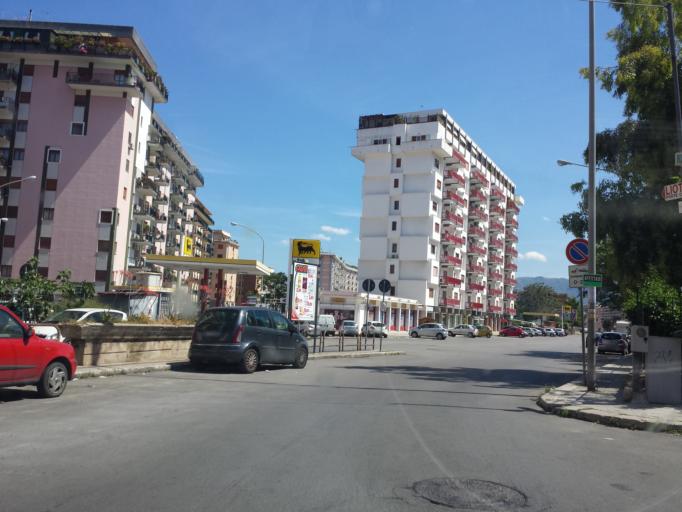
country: IT
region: Sicily
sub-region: Palermo
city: Palermo
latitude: 38.1397
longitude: 13.3351
